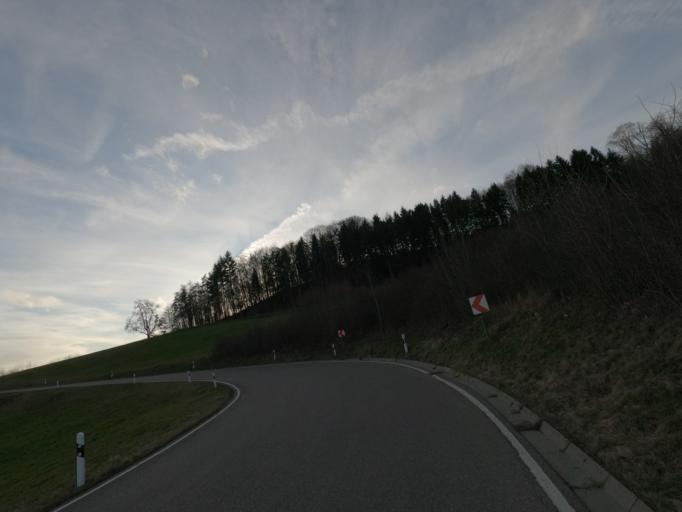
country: DE
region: Baden-Wuerttemberg
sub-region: Regierungsbezirk Stuttgart
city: Ottenbach
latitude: 48.7474
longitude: 9.7507
